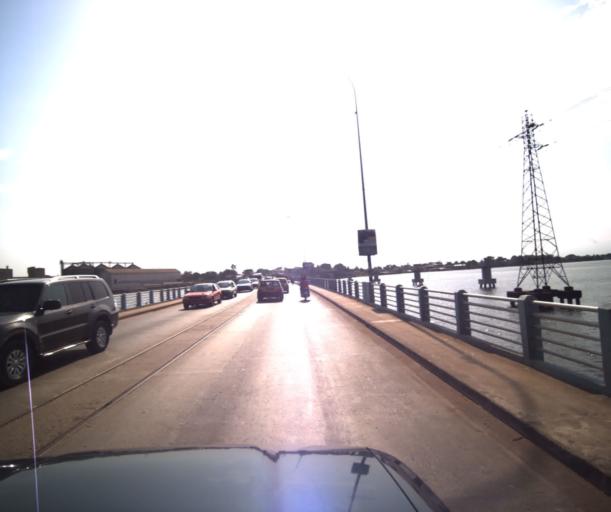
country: CM
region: Littoral
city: Bonaberi
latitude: 4.0725
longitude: 9.6937
